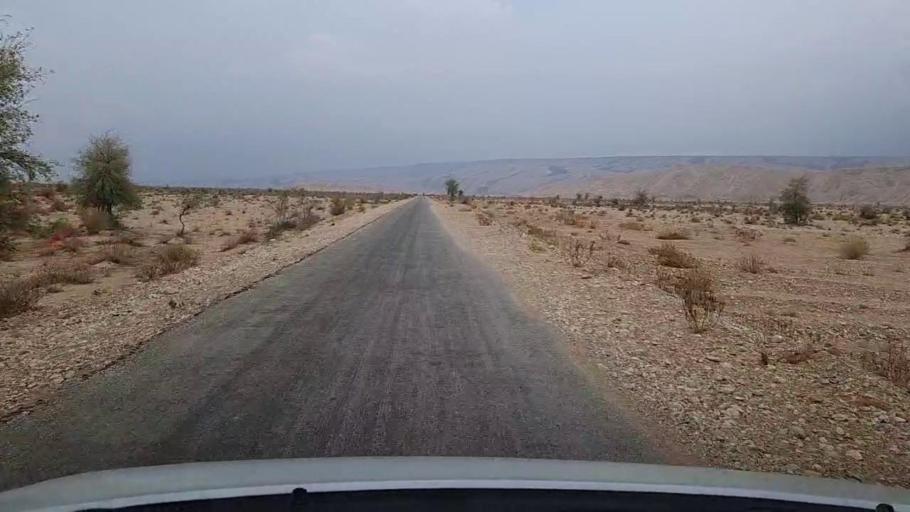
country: PK
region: Sindh
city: Sehwan
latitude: 26.2554
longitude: 67.7207
